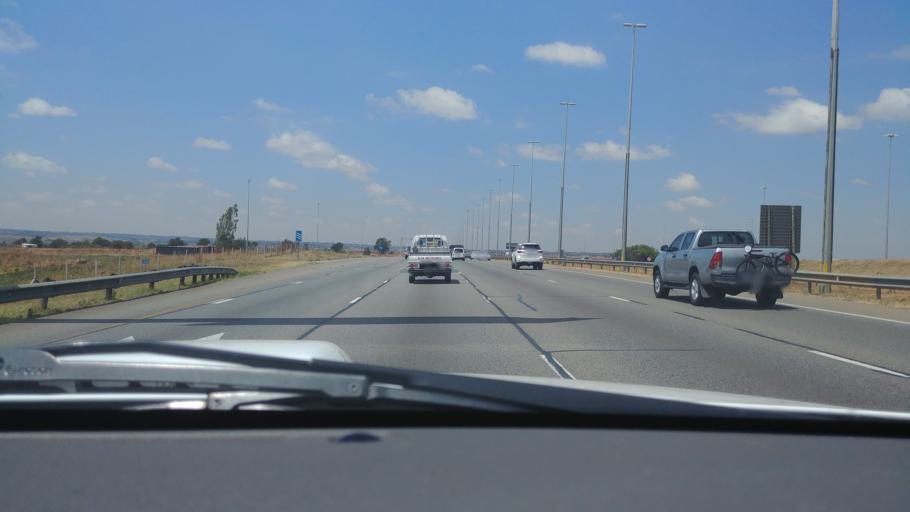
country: ZA
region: Gauteng
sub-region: Ekurhuleni Metropolitan Municipality
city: Tembisa
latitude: -26.0282
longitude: 28.2638
